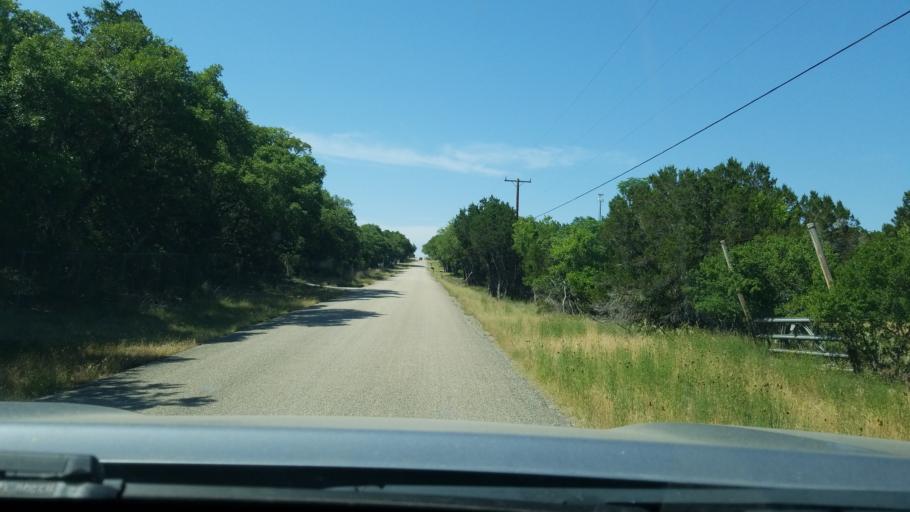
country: US
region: Texas
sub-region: Comal County
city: Bulverde
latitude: 29.7602
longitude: -98.5153
